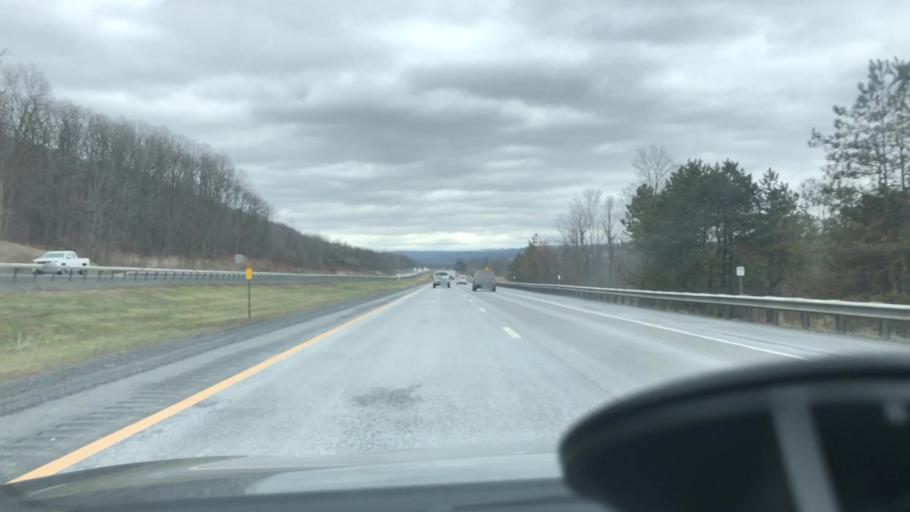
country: US
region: New York
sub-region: Herkimer County
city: Frankfort
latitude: 43.0460
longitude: -75.0575
